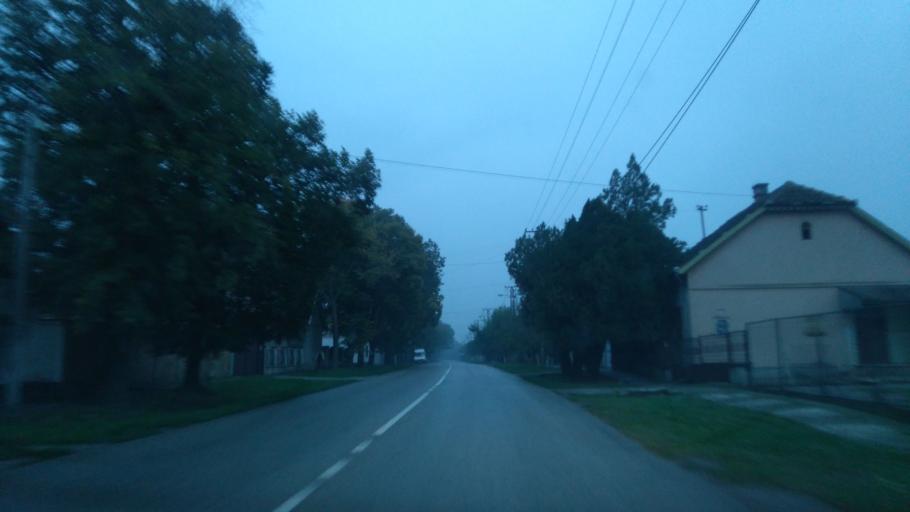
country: RS
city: Backo Petrovo Selo
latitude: 45.6944
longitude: 20.0817
